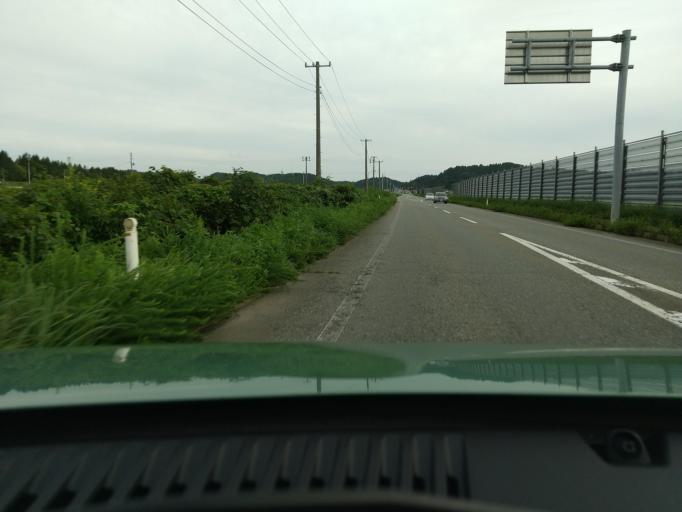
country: JP
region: Akita
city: Akita Shi
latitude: 39.8042
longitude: 140.0949
